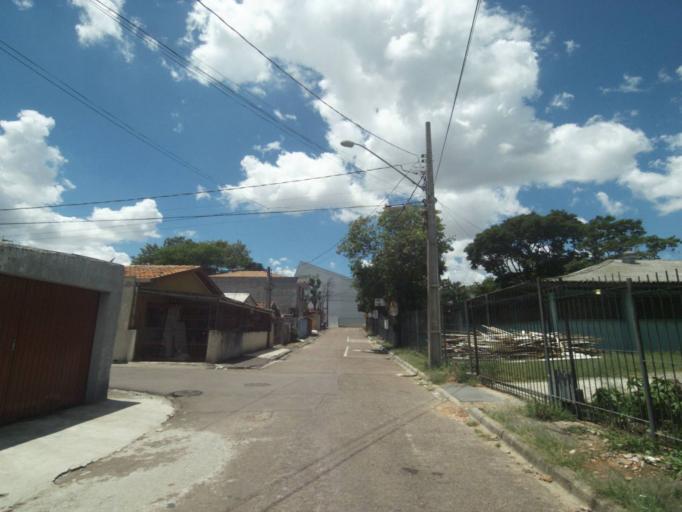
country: BR
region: Parana
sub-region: Curitiba
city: Curitiba
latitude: -25.5046
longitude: -49.3251
